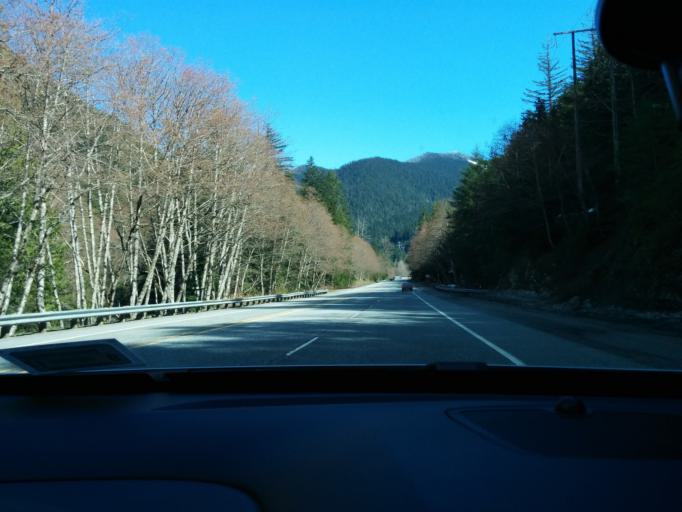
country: US
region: Washington
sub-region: Chelan County
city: Leavenworth
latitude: 47.7144
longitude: -121.1741
